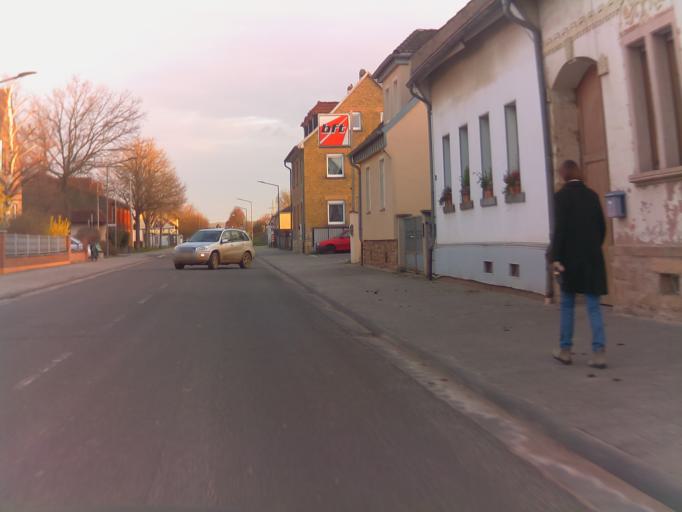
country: DE
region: Rheinland-Pfalz
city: Wallertheim
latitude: 49.8321
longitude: 8.0531
